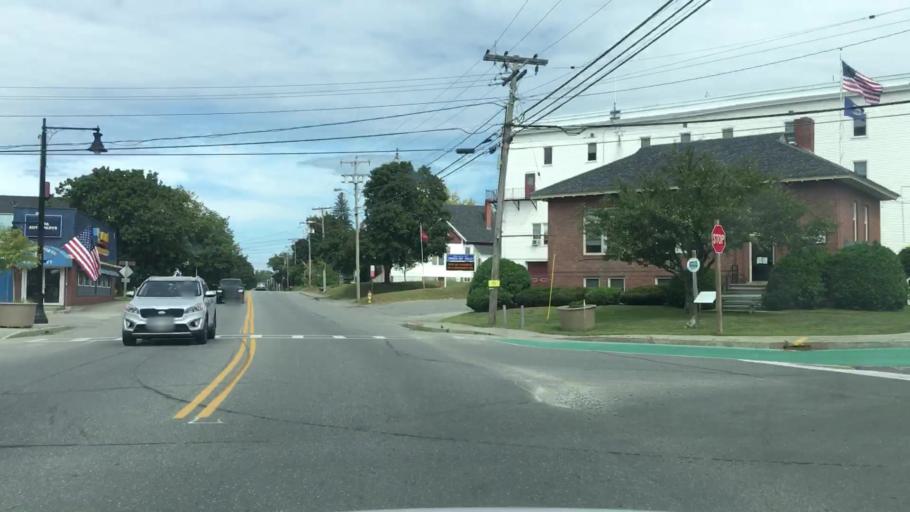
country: US
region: Maine
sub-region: Piscataquis County
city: Milo
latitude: 45.2533
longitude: -68.9862
